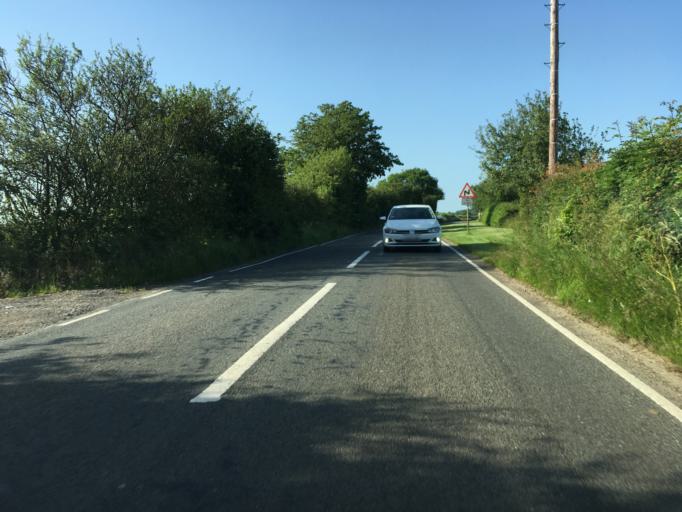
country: GB
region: England
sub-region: Oxfordshire
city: Charlbury
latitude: 51.8848
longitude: -1.4749
